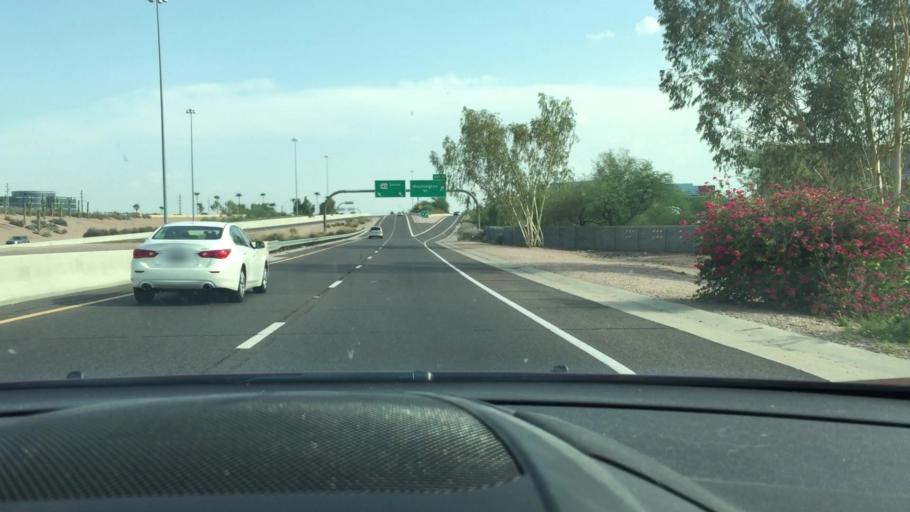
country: US
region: Arizona
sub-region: Maricopa County
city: Tempe Junction
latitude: 33.4548
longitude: -111.9834
